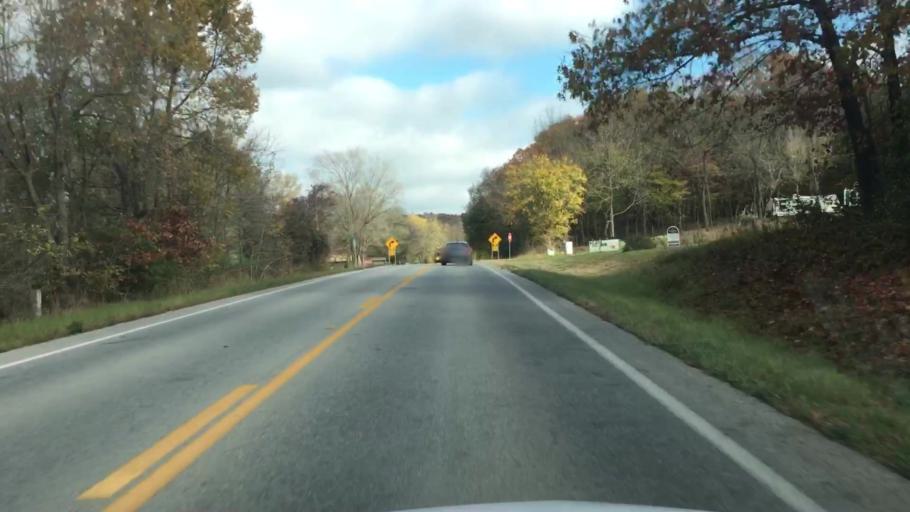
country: US
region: Arkansas
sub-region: Benton County
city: Gentry
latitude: 36.2591
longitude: -94.4250
